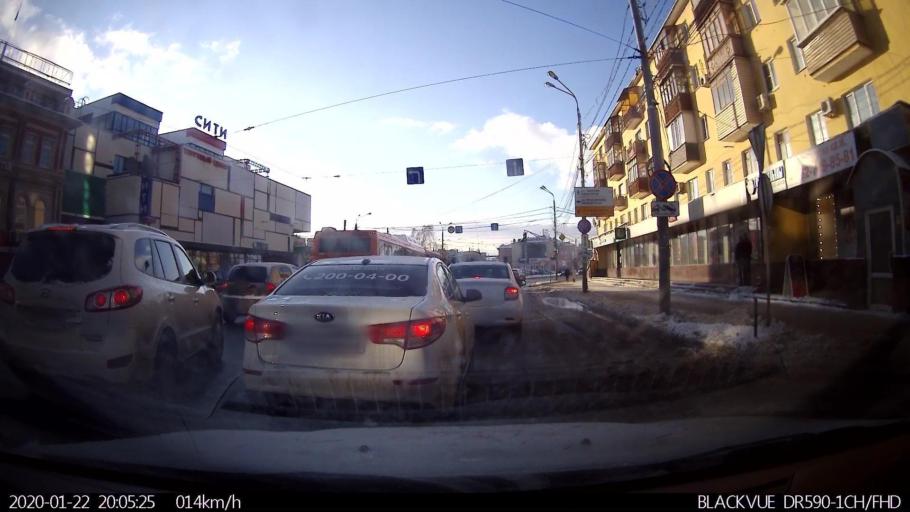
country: RU
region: Nizjnij Novgorod
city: Nizhniy Novgorod
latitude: 56.3201
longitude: 43.9448
